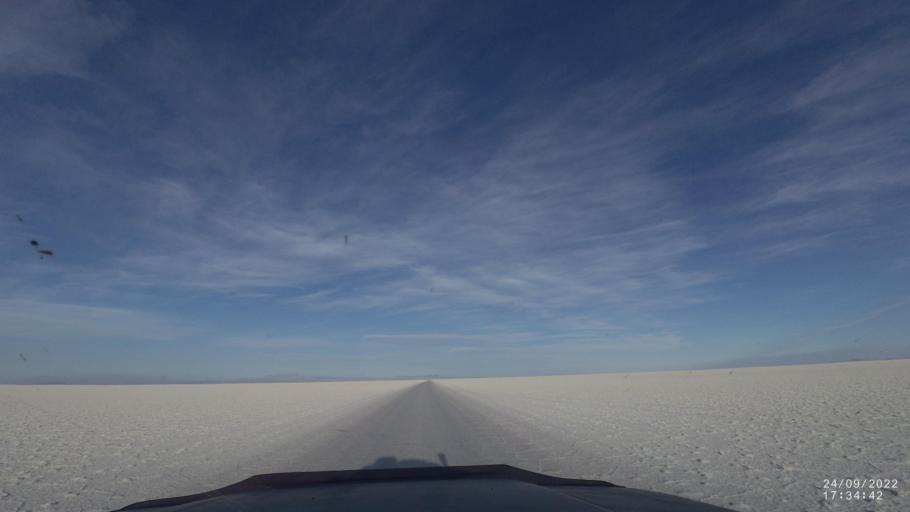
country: BO
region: Potosi
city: Colchani
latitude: -20.3219
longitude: -67.2754
